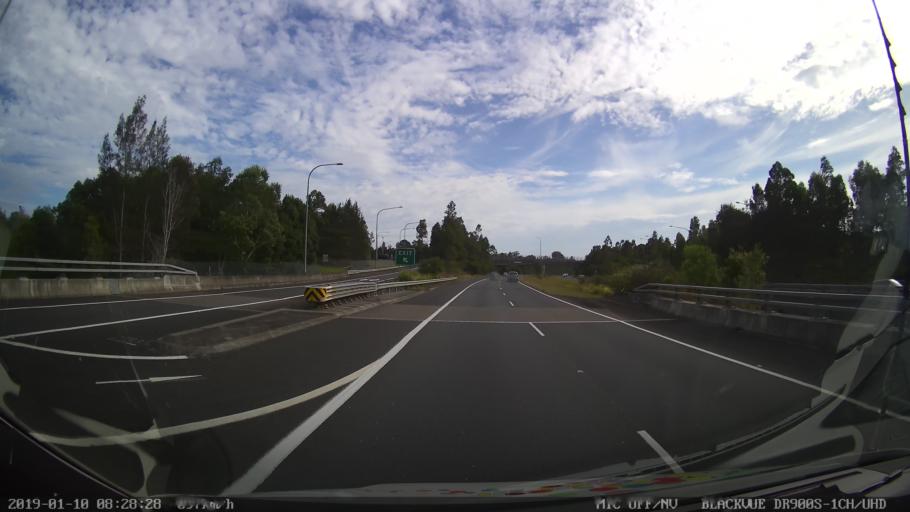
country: AU
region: New South Wales
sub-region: Coffs Harbour
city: Bonville
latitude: -30.3928
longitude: 153.0332
